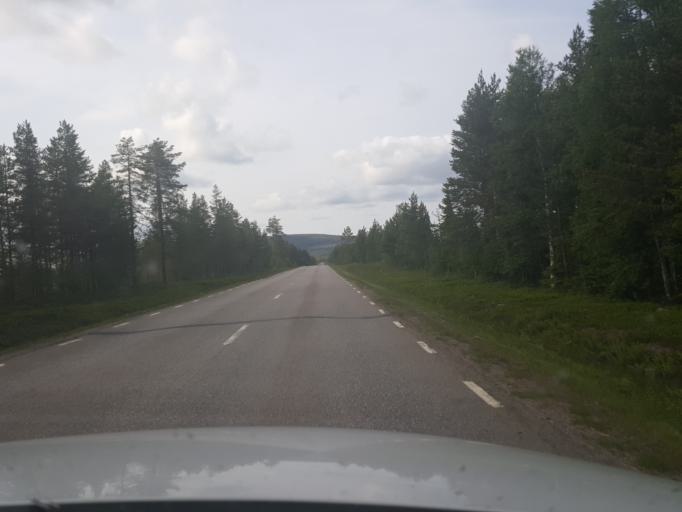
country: SE
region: Norrbotten
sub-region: Arjeplogs Kommun
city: Arjeplog
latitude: 65.6176
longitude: 18.0810
